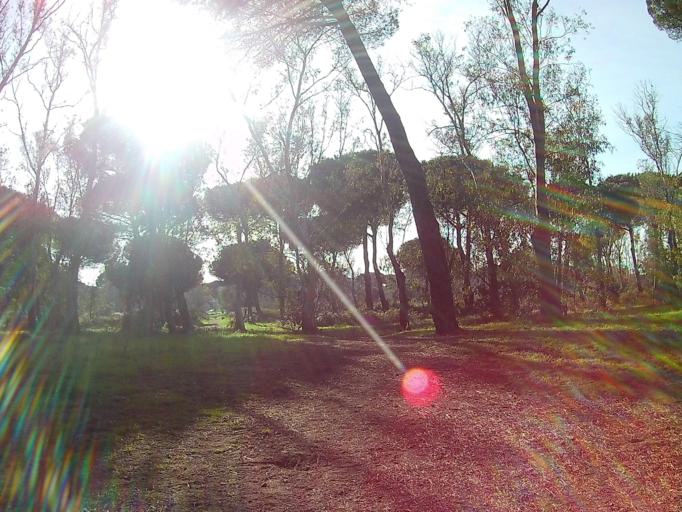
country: IT
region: Latium
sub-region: Citta metropolitana di Roma Capitale
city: Lido di Ostia
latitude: 41.7444
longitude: 12.2709
